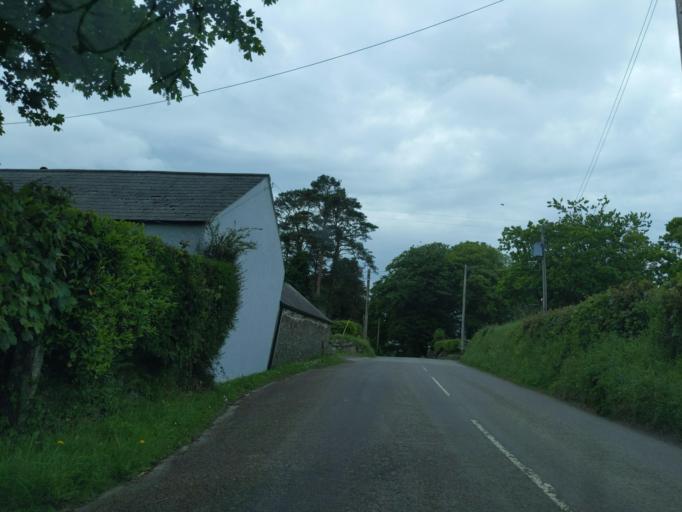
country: GB
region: England
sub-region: Devon
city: Horrabridge
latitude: 50.5185
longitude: -4.1081
